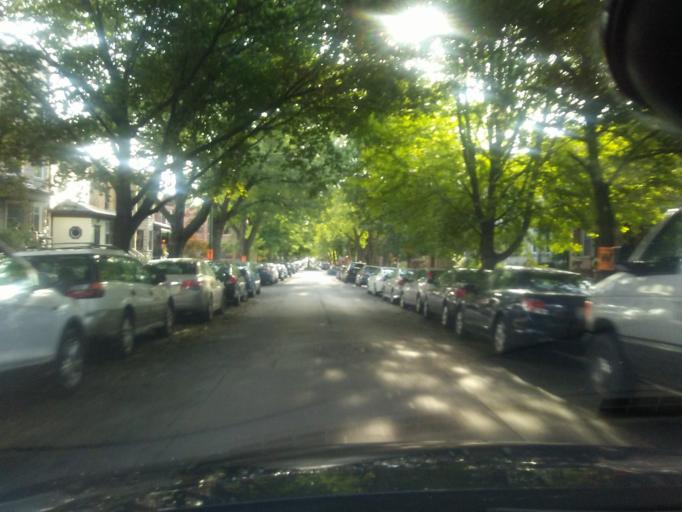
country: US
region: Illinois
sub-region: Cook County
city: Evanston
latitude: 41.9799
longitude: -87.6664
